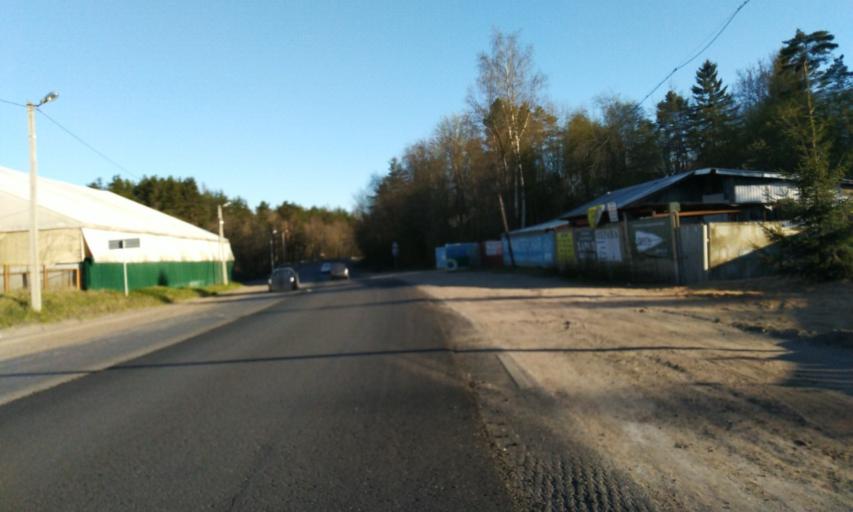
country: RU
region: Leningrad
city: Toksovo
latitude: 60.1407
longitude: 30.5291
